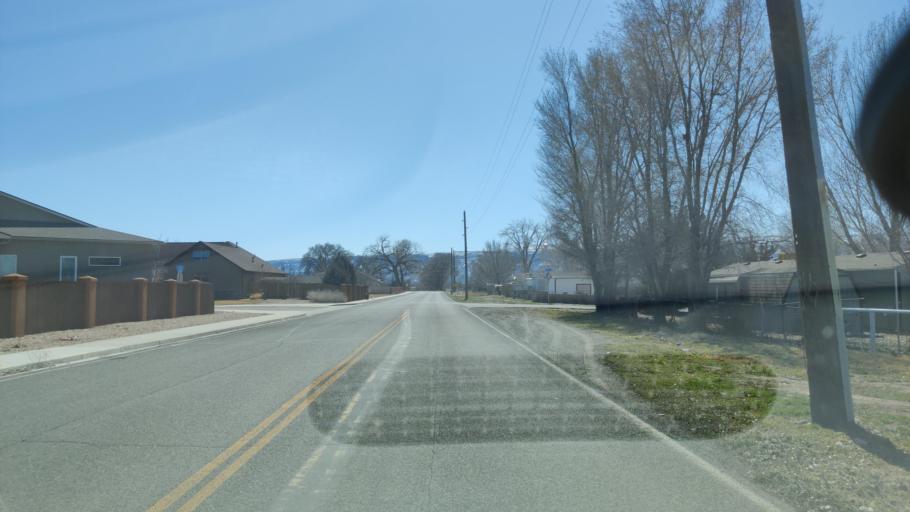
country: US
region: Colorado
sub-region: Mesa County
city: Fruita
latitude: 39.1667
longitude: -108.7104
